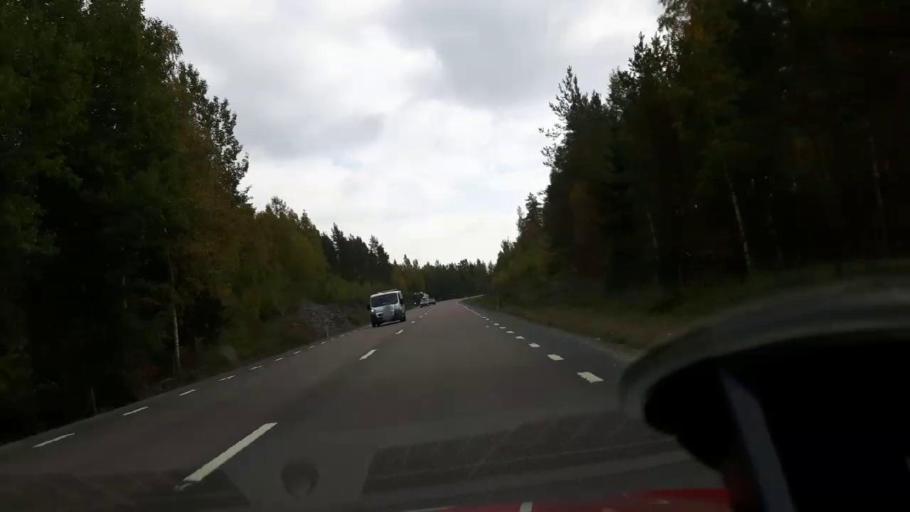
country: SE
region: Gaevleborg
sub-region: Bollnas Kommun
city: Kilafors
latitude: 61.2719
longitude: 16.5342
